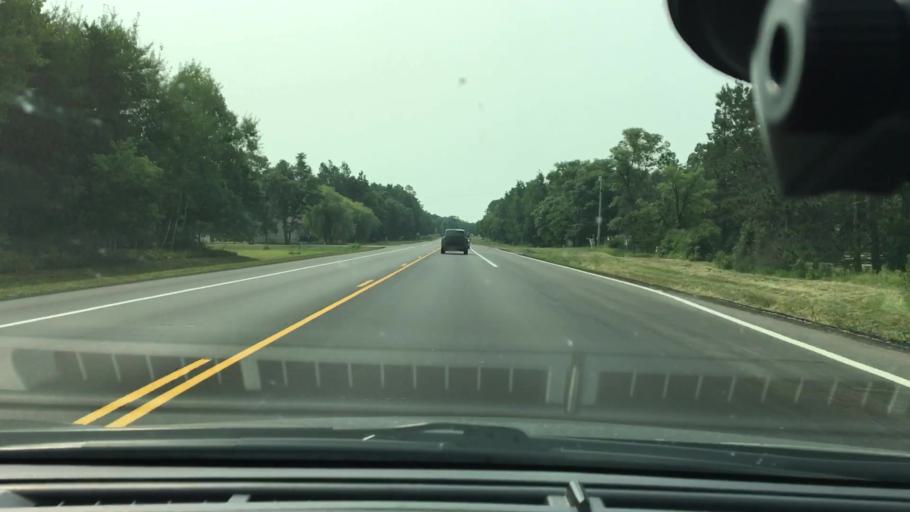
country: US
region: Minnesota
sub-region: Crow Wing County
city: Brainerd
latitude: 46.4434
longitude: -94.1718
